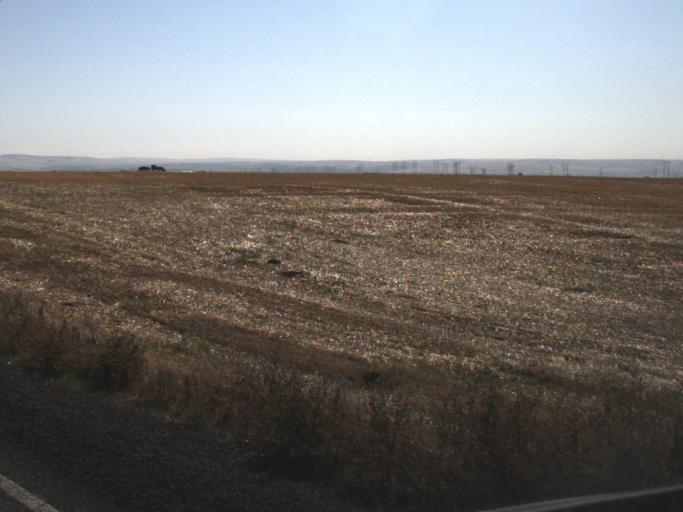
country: US
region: Washington
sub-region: Walla Walla County
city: Walla Walla
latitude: 46.0987
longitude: -118.3705
